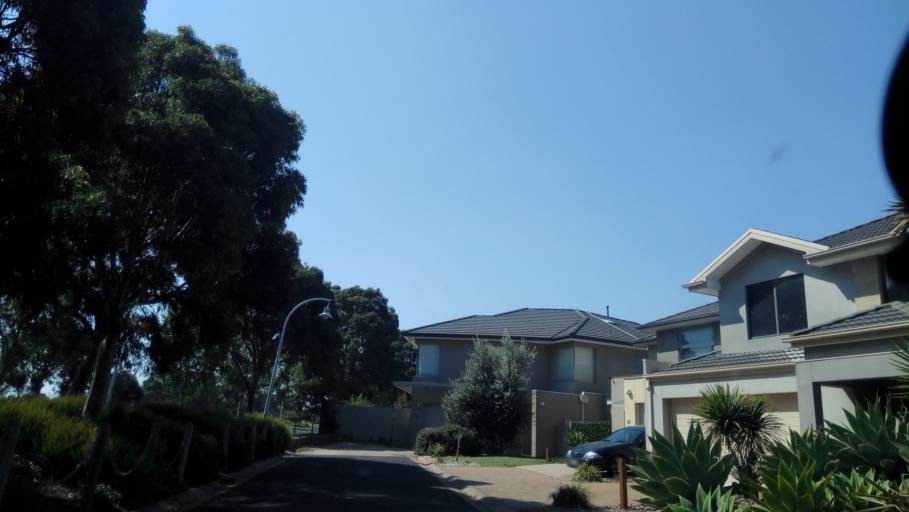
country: AU
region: Victoria
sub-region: Hobsons Bay
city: Altona Meadows
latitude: -37.8918
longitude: 144.7615
